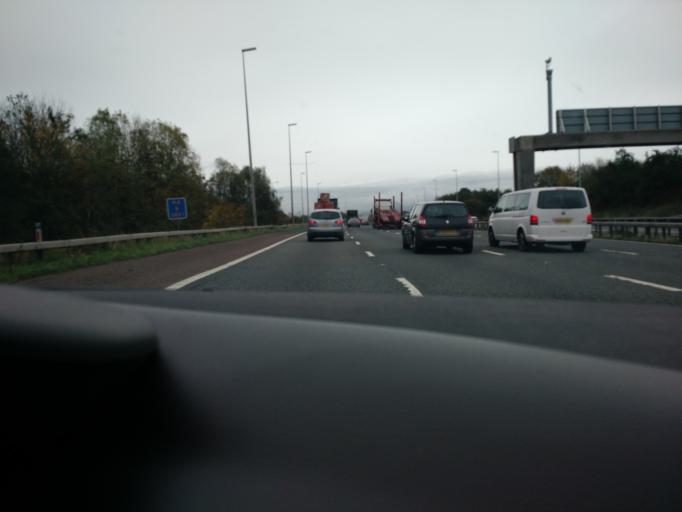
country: GB
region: England
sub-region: Lancashire
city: Goosnargh
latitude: 53.7901
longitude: -2.6605
